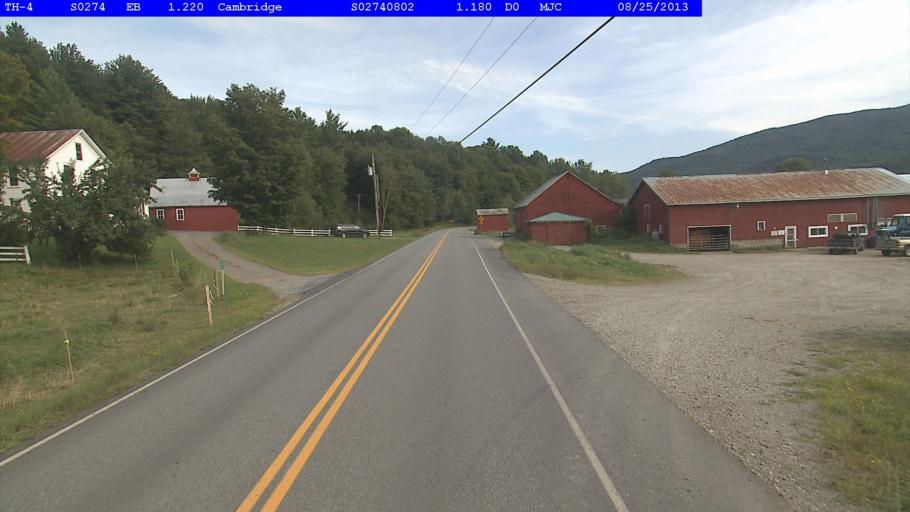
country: US
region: Vermont
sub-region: Lamoille County
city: Johnson
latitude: 44.6678
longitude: -72.7616
